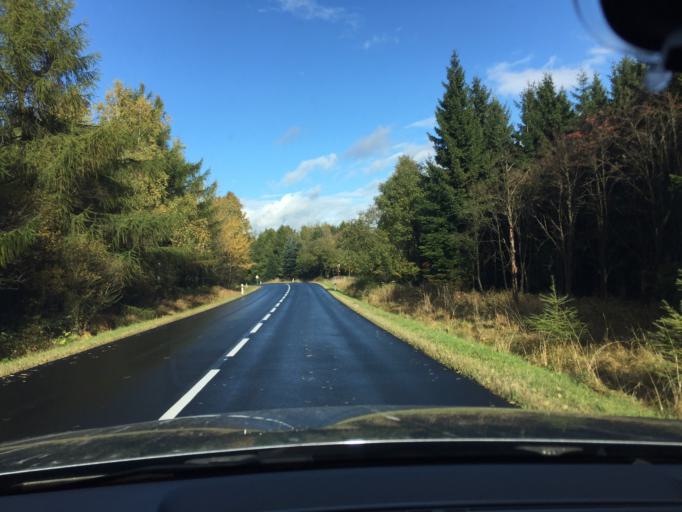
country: CZ
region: Ustecky
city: Libouchec
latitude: 50.7584
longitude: 13.9751
